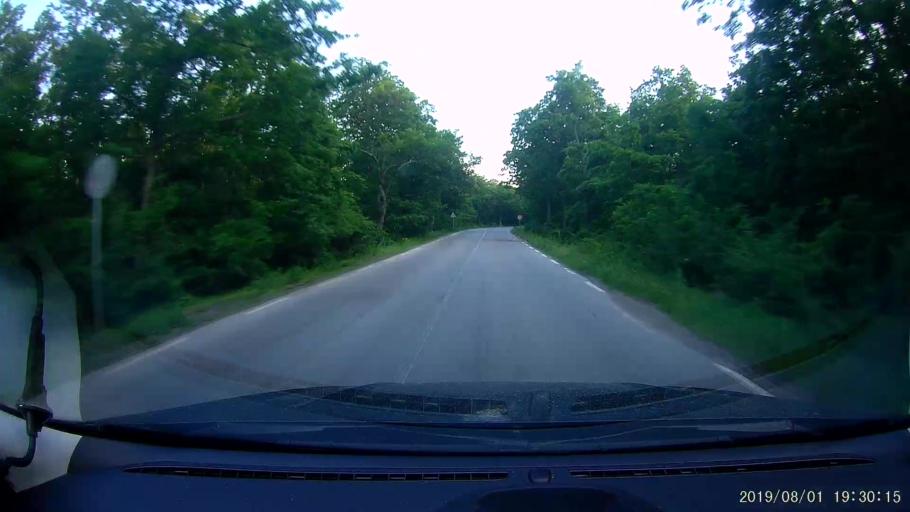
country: BG
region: Burgas
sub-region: Obshtina Sungurlare
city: Sungurlare
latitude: 42.8165
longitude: 26.8944
